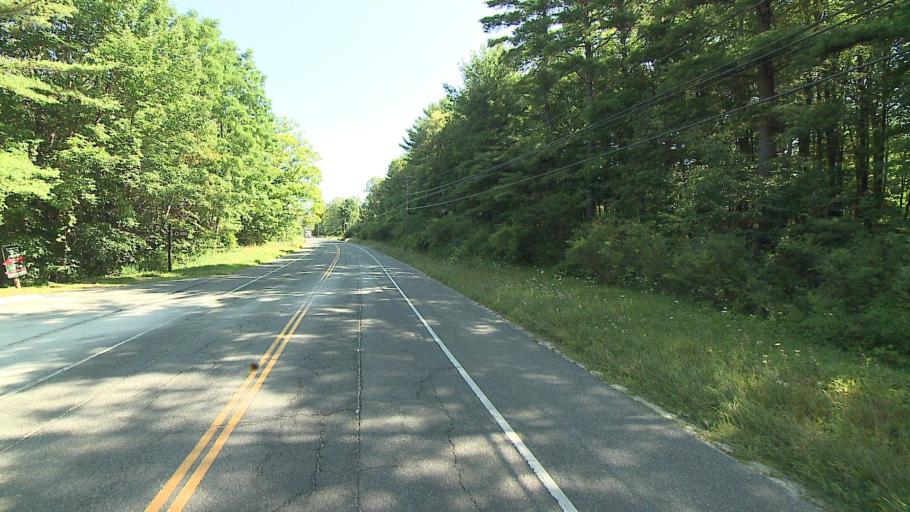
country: US
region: Connecticut
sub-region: Litchfield County
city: Canaan
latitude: 41.9364
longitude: -73.4406
